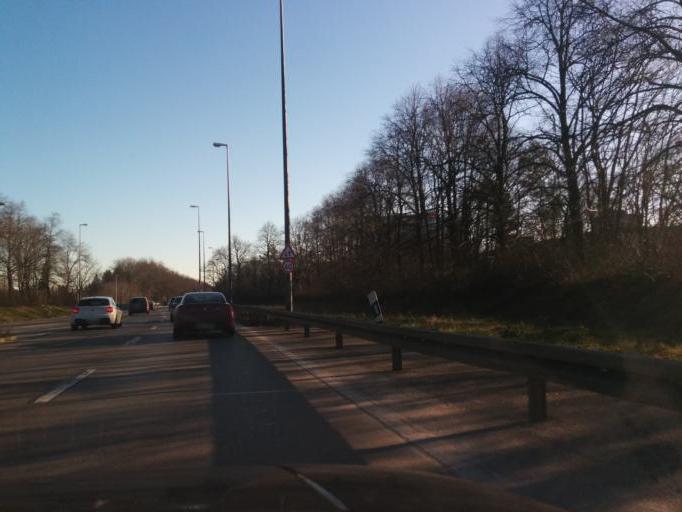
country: DE
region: Bavaria
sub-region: Upper Bavaria
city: Unterhaching
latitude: 48.1058
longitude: 11.6195
